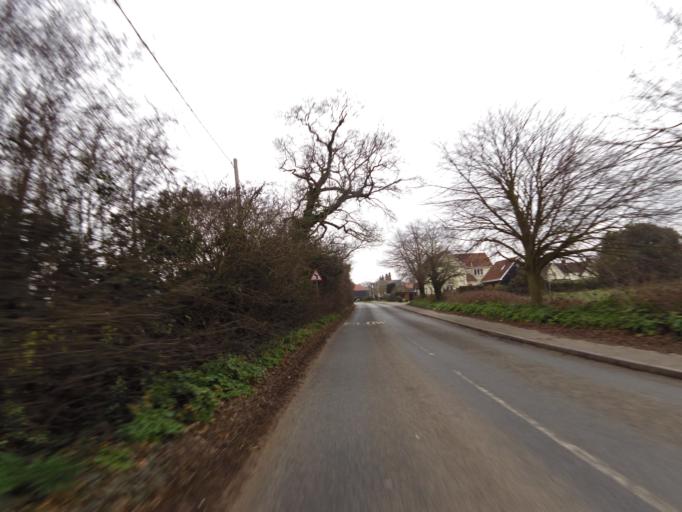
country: GB
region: England
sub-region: Suffolk
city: Wickham Market
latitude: 52.1514
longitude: 1.3965
